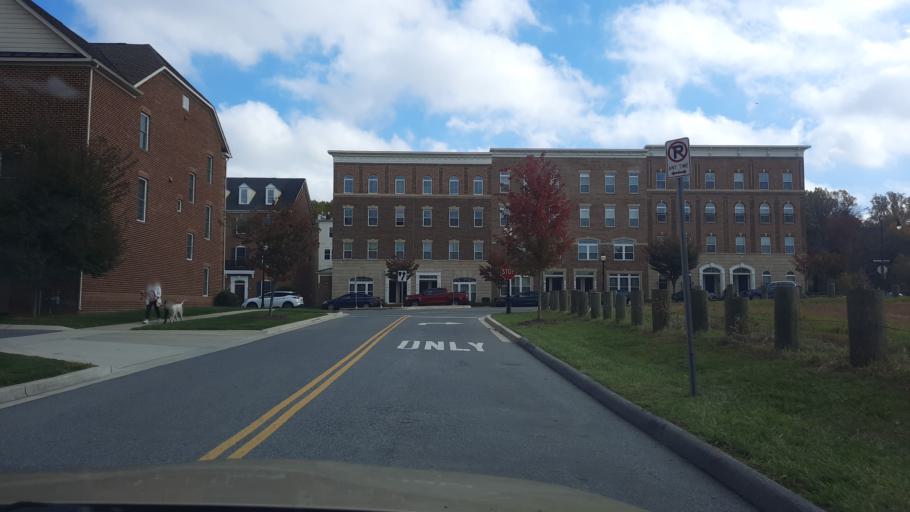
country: US
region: Maryland
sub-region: Montgomery County
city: Gaithersburg
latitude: 39.1518
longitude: -77.2257
